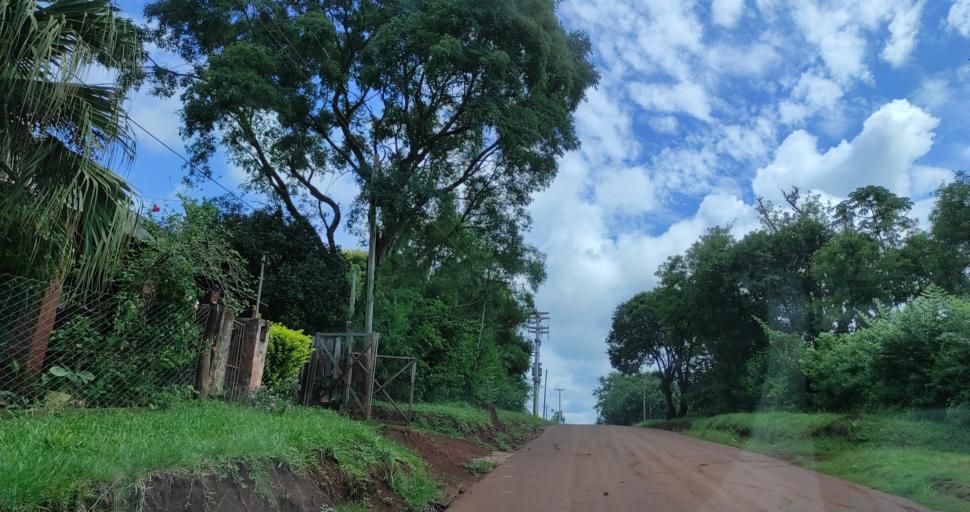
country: AR
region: Corrientes
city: San Carlos
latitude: -27.7494
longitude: -55.8914
